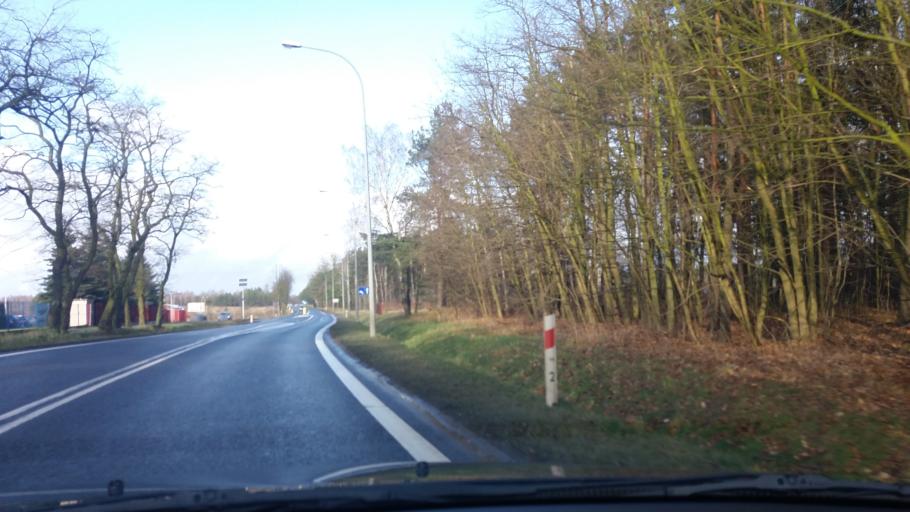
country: PL
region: Masovian Voivodeship
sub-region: Powiat przasnyski
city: Chorzele
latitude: 53.2672
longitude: 20.8975
